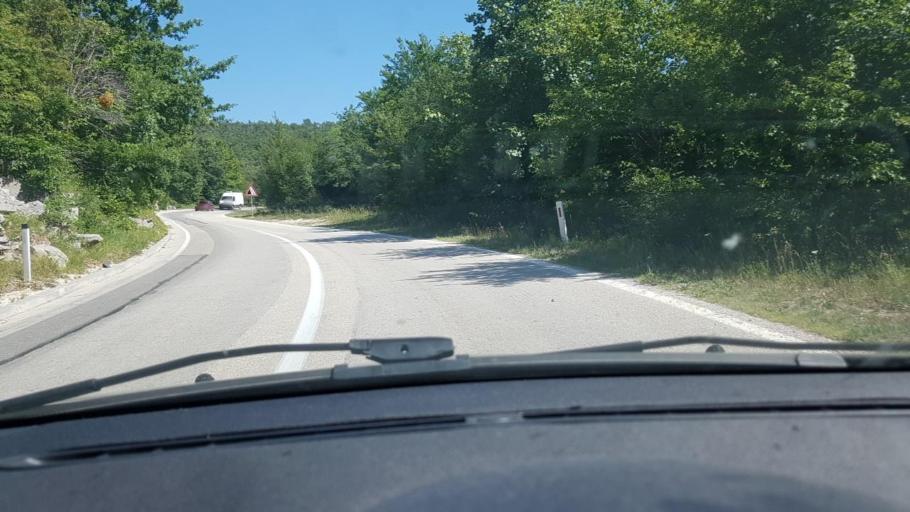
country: BA
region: Federation of Bosnia and Herzegovina
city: Bosansko Grahovo
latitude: 44.3115
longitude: 16.3124
